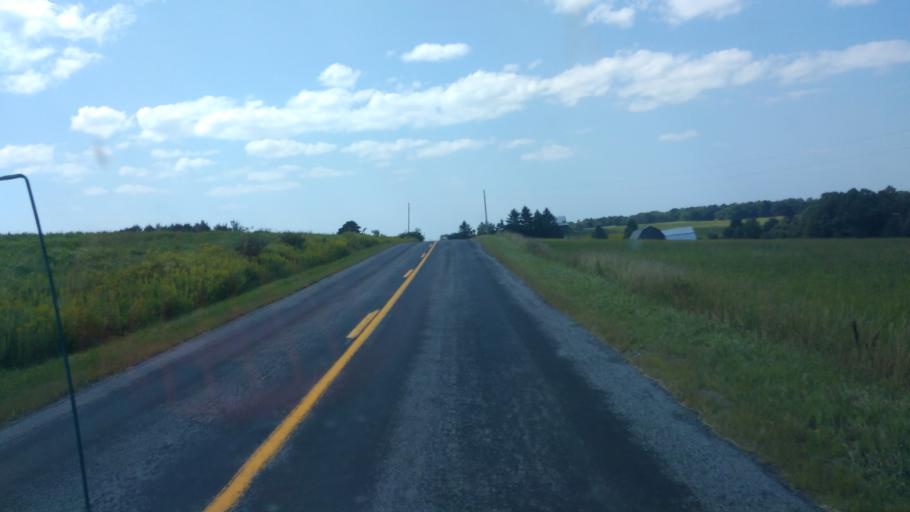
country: US
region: New York
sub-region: Steuben County
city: Canisteo
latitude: 42.3538
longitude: -77.5601
